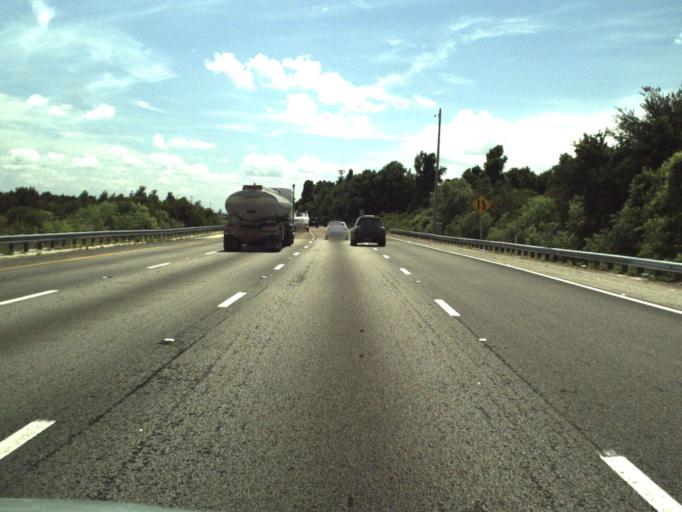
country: US
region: Florida
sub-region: Volusia County
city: Deltona
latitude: 28.8999
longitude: -81.2765
